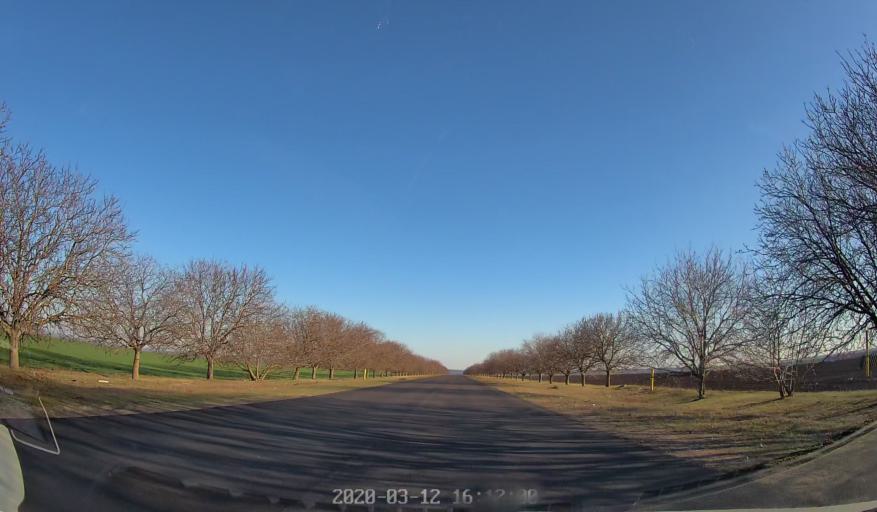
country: MD
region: Anenii Noi
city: Anenii Noi
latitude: 46.9410
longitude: 29.2669
